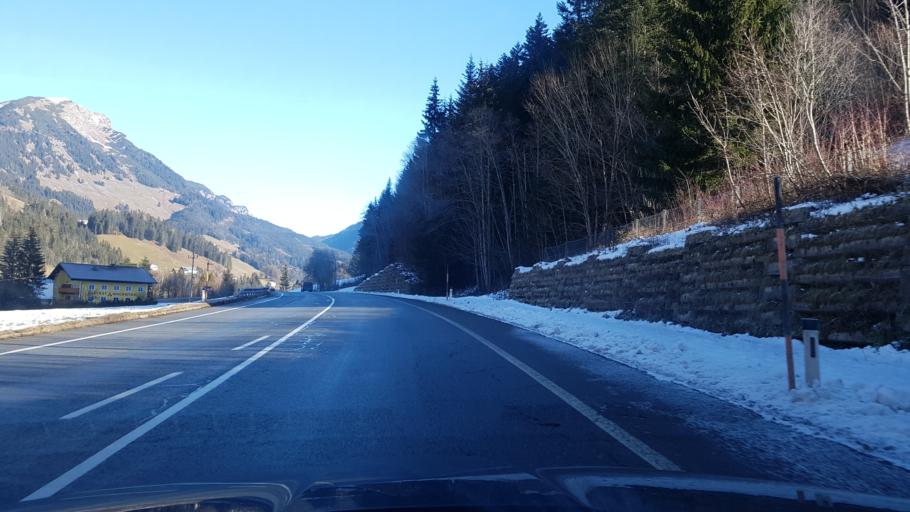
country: AT
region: Salzburg
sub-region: Politischer Bezirk Hallein
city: Abtenau
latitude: 47.5804
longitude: 13.4490
